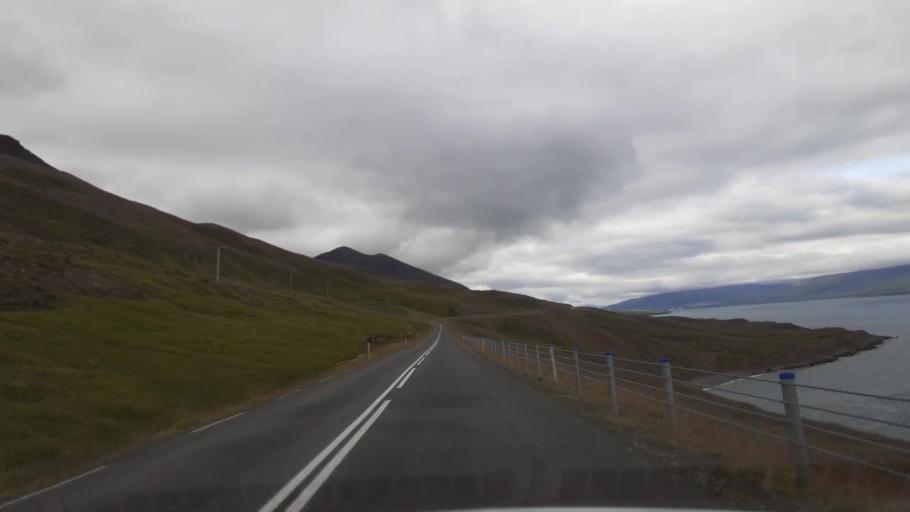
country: IS
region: Northeast
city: Akureyri
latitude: 65.8406
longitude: -18.0565
